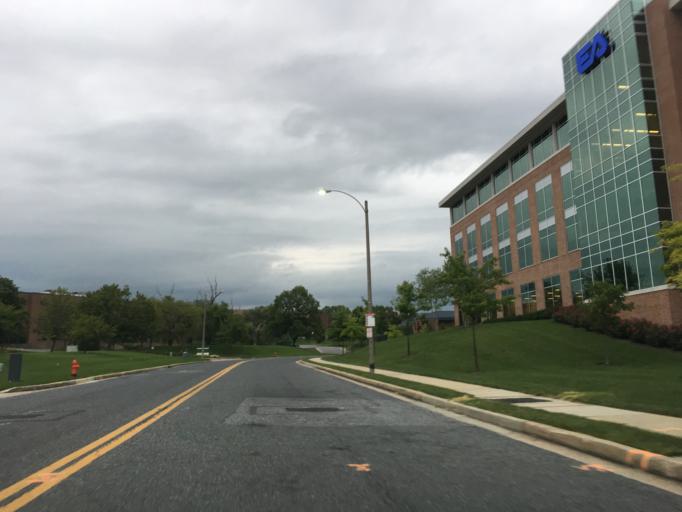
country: US
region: Maryland
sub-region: Baltimore County
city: Cockeysville
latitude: 39.4904
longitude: -76.6643
